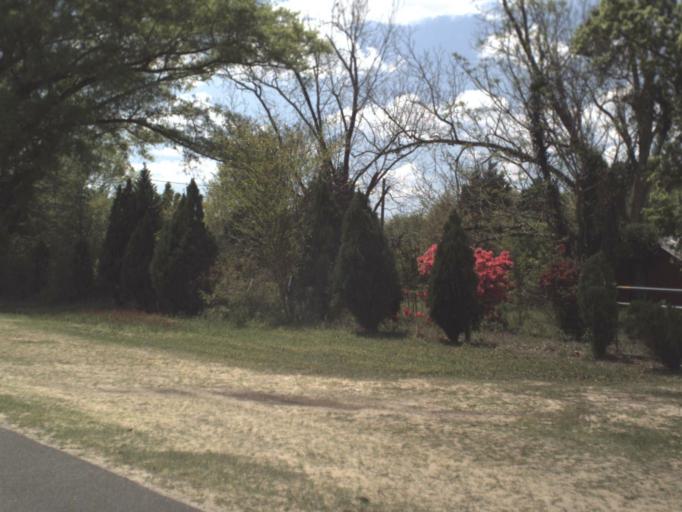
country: US
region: Florida
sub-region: Okaloosa County
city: Crestview
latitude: 30.8547
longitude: -86.6750
